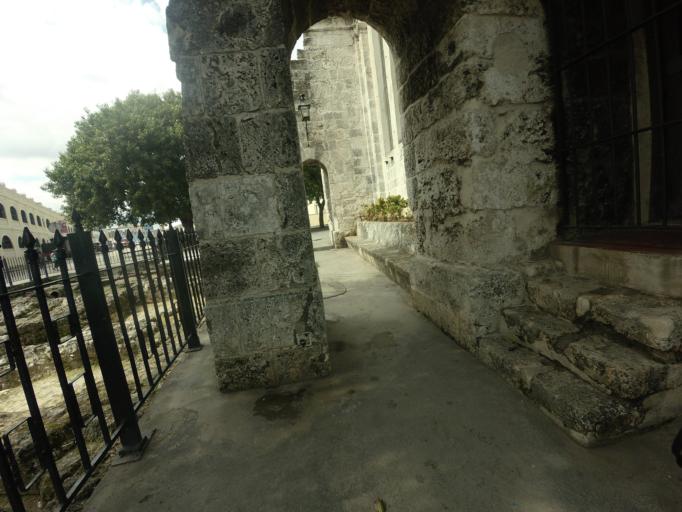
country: CU
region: La Habana
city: La Habana Vieja
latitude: 23.1309
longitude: -82.3486
